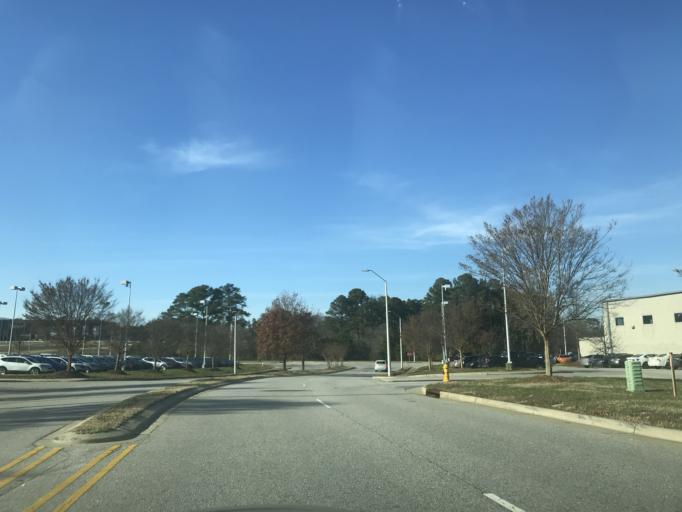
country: US
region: North Carolina
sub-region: Wake County
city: Wake Forest
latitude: 35.8856
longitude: -78.5687
